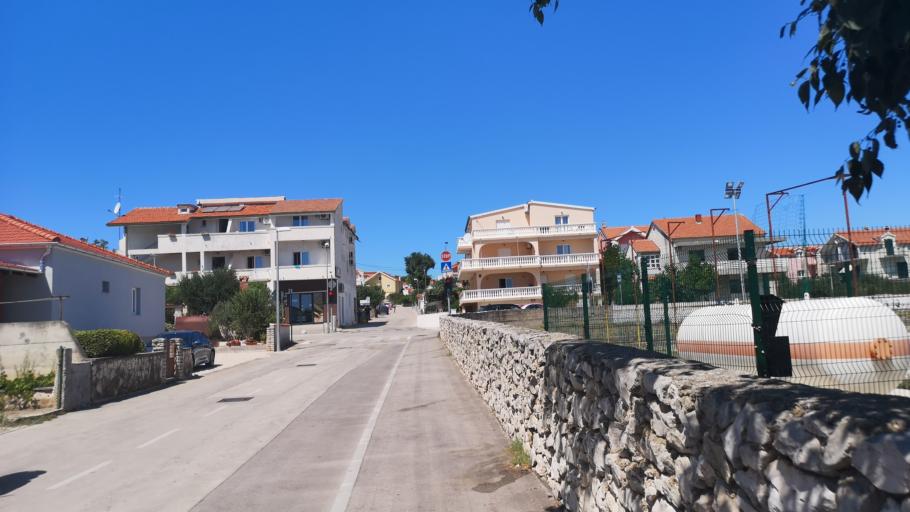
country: HR
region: Sibensko-Kniniska
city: Vodice
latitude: 43.7600
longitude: 15.7706
